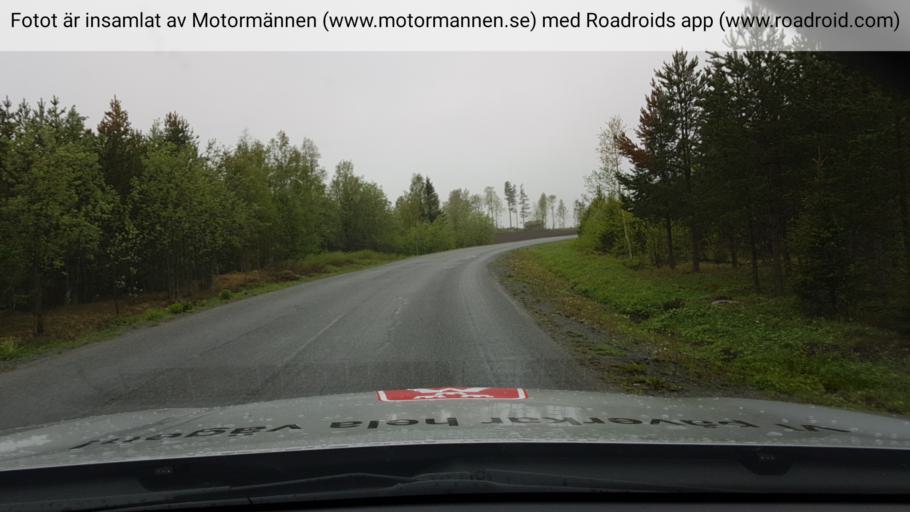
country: SE
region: Jaemtland
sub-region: Bergs Kommun
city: Hoverberg
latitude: 62.9784
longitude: 14.3215
